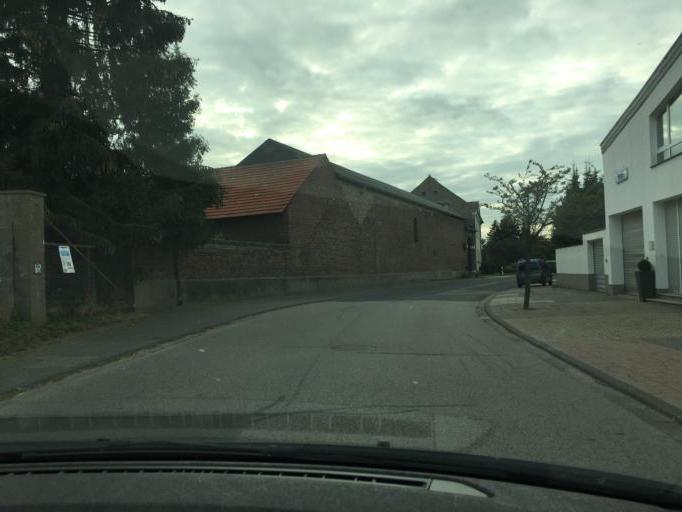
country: DE
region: North Rhine-Westphalia
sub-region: Regierungsbezirk Koln
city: Merzenich
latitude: 50.8557
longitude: 6.5847
